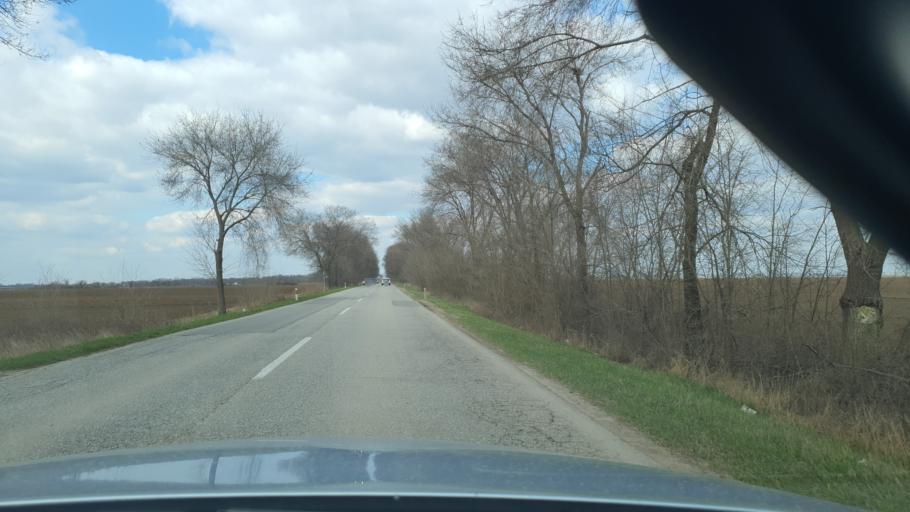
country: RS
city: Obrovac
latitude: 45.4364
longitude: 19.3756
